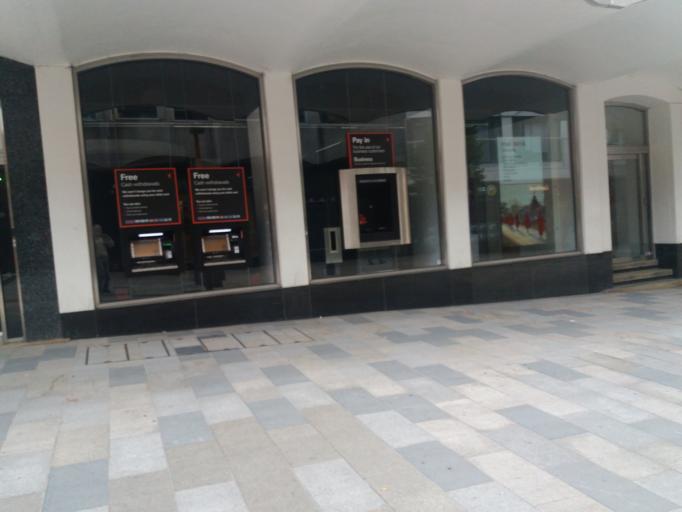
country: GB
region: England
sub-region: Bracknell Forest
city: Bracknell
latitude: 51.4164
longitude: -0.7476
